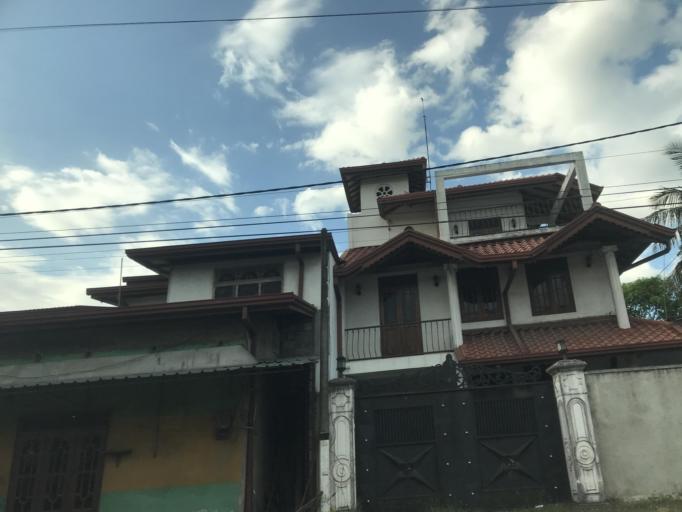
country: LK
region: Western
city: Gampaha
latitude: 7.0545
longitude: 80.0069
